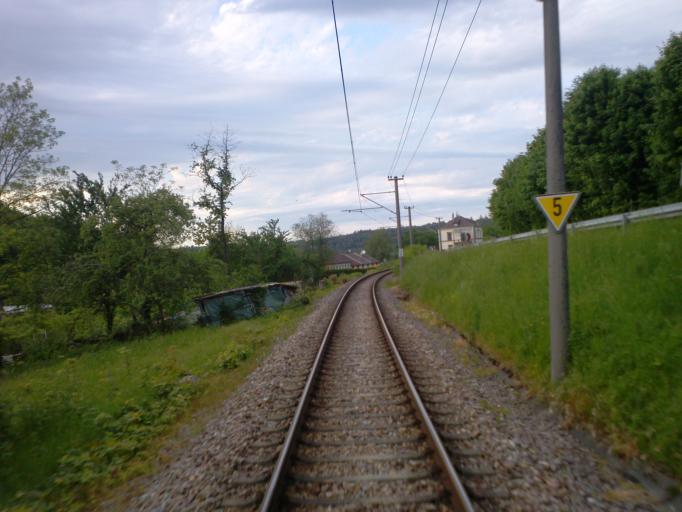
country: DE
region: Baden-Wuerttemberg
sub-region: Karlsruhe Region
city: Ettlingen
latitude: 48.9099
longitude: 8.4541
